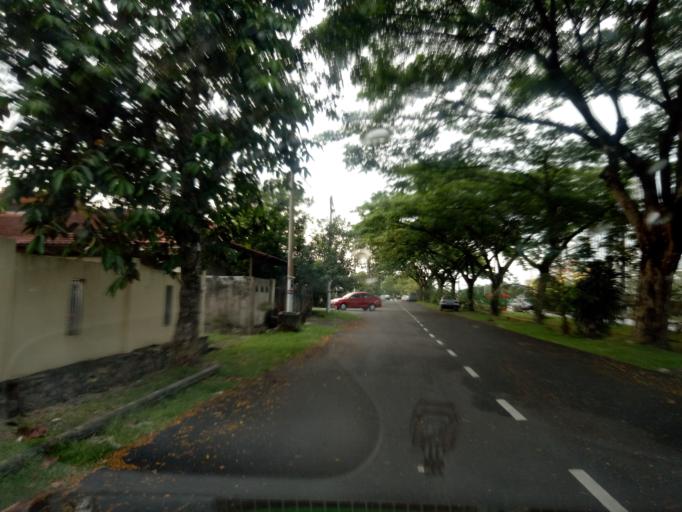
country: MY
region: Selangor
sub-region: Hulu Langat
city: Semenyih
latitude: 2.9278
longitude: 101.8601
